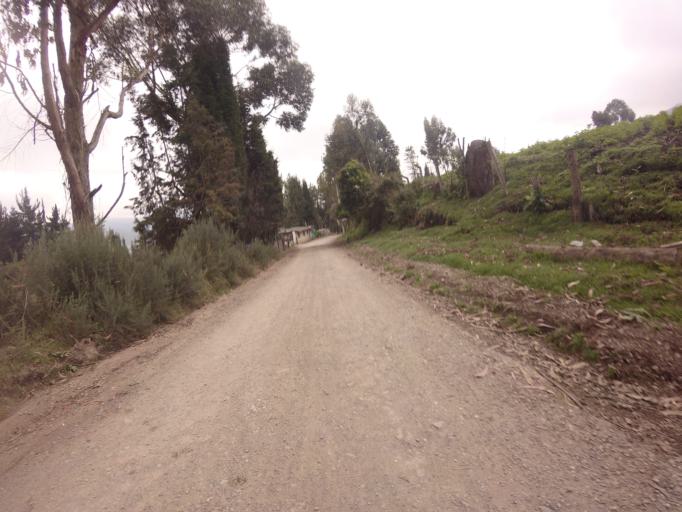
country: CO
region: Cundinamarca
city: Cogua
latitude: 5.1441
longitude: -73.9561
